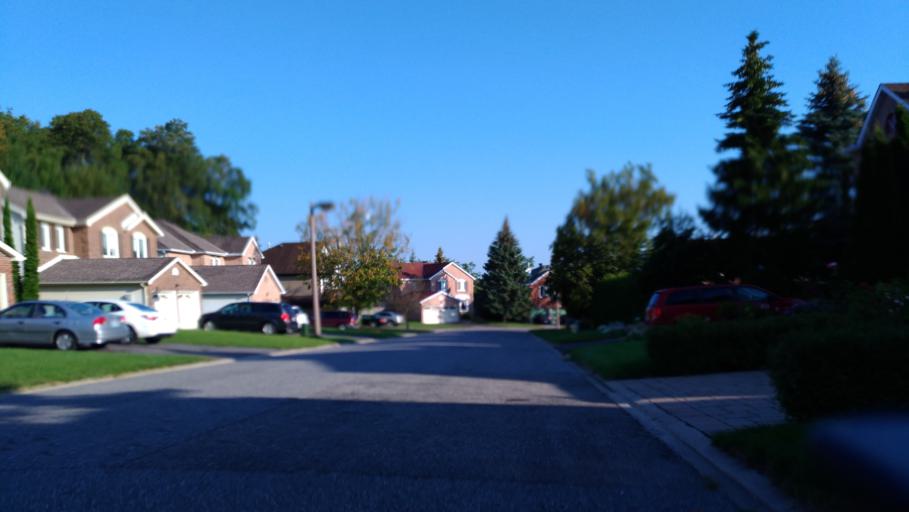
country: CA
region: Ontario
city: Bells Corners
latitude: 45.3482
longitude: -75.9304
